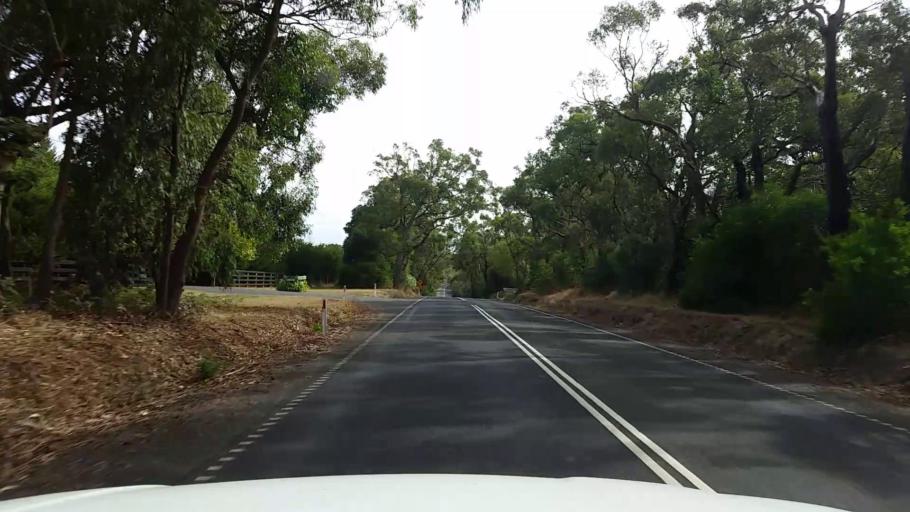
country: AU
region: Victoria
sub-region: Mornington Peninsula
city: Mount Martha
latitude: -38.2982
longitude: 145.0783
